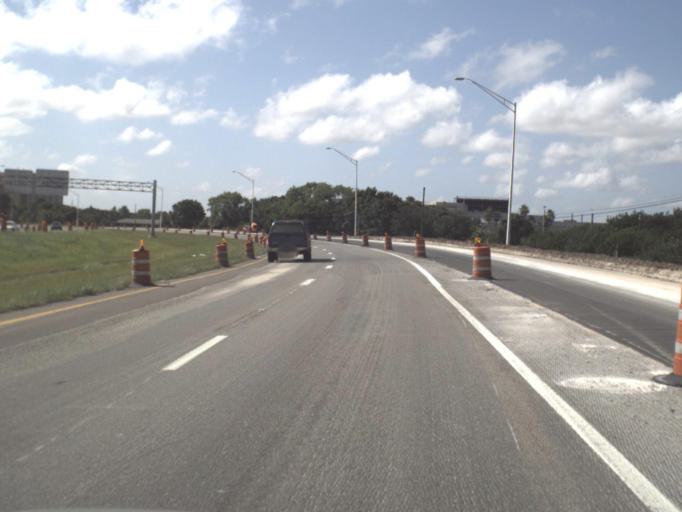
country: US
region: Florida
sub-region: Pinellas County
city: Feather Sound
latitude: 27.8910
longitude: -82.6737
